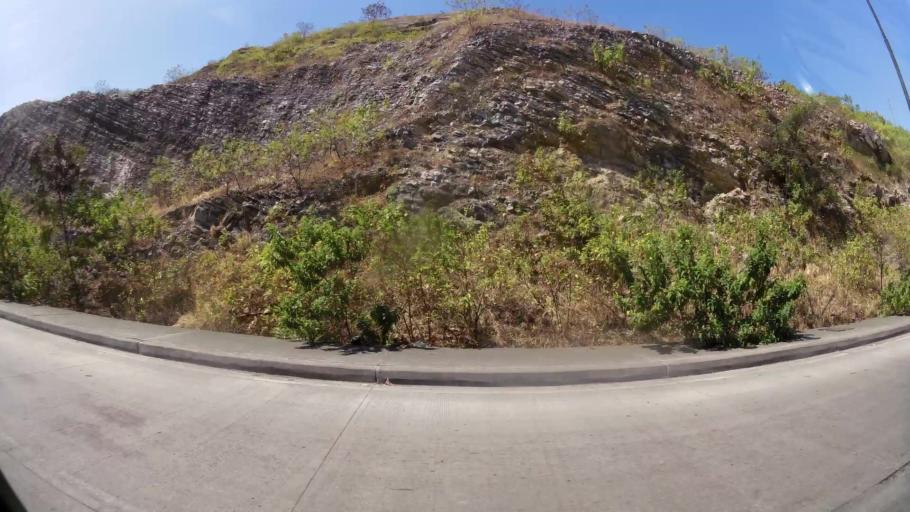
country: EC
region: Guayas
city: Guayaquil
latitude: -2.1848
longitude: -79.9318
